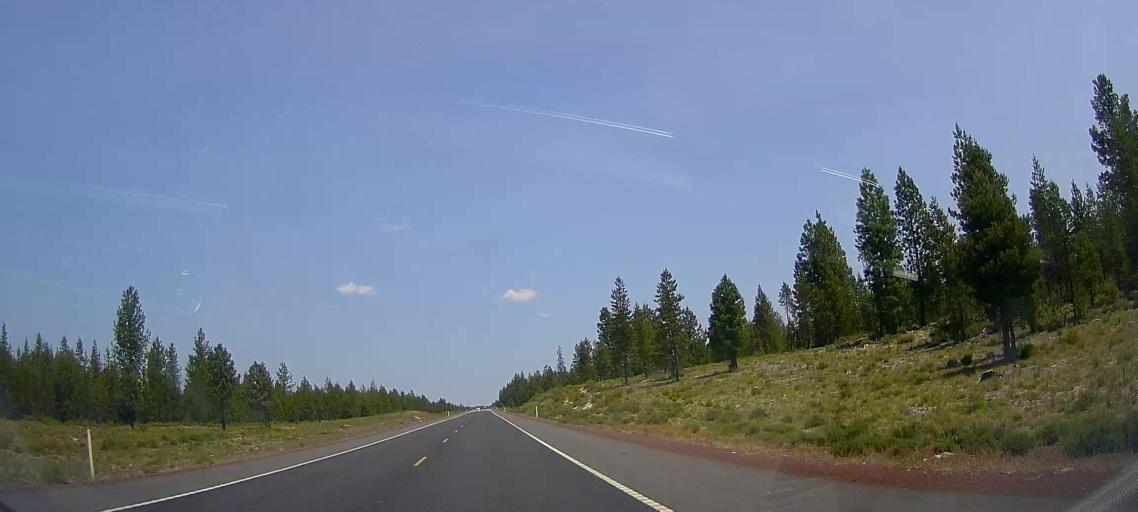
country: US
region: Oregon
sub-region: Deschutes County
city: La Pine
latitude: 43.5076
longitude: -121.6615
